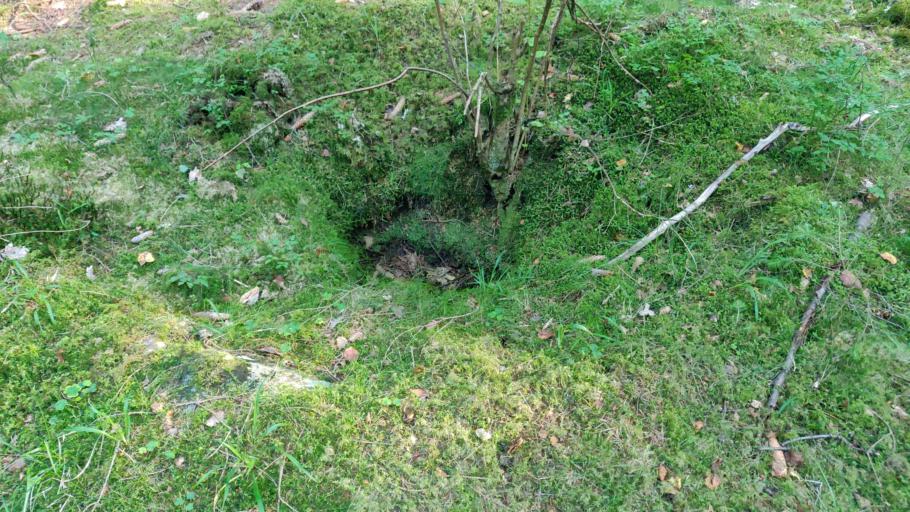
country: SE
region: Vaestra Goetaland
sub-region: Uddevalla Kommun
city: Uddevalla
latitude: 58.3722
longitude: 11.9584
